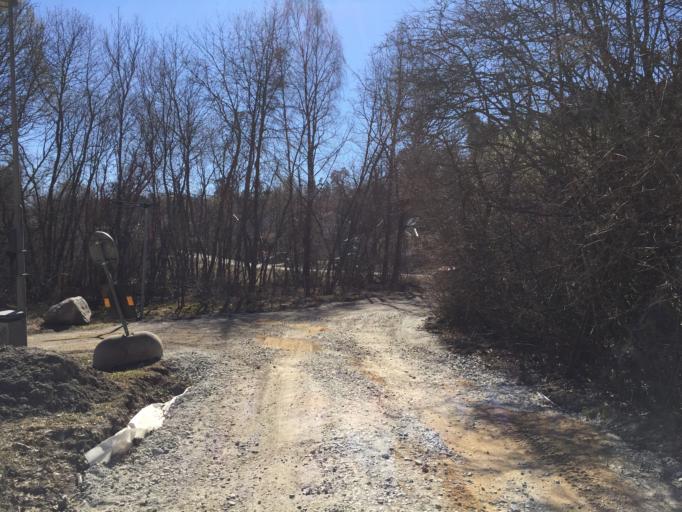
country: SE
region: Stockholm
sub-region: Salems Kommun
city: Ronninge
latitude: 59.2005
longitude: 17.7169
